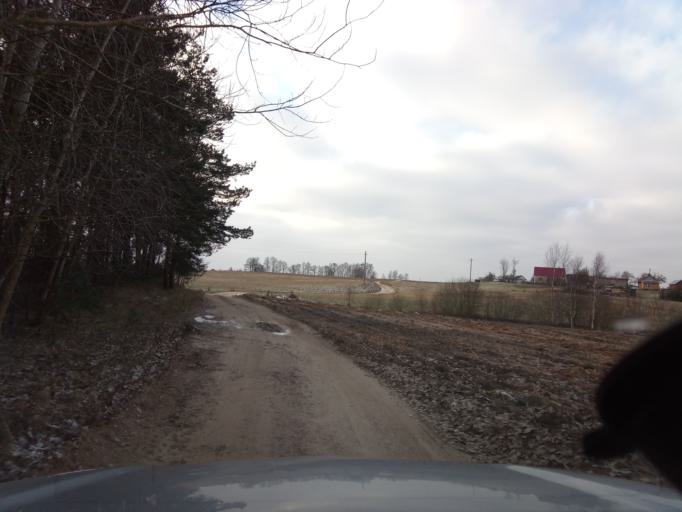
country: LT
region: Alytaus apskritis
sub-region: Alytaus rajonas
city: Daugai
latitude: 54.3761
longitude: 24.3939
